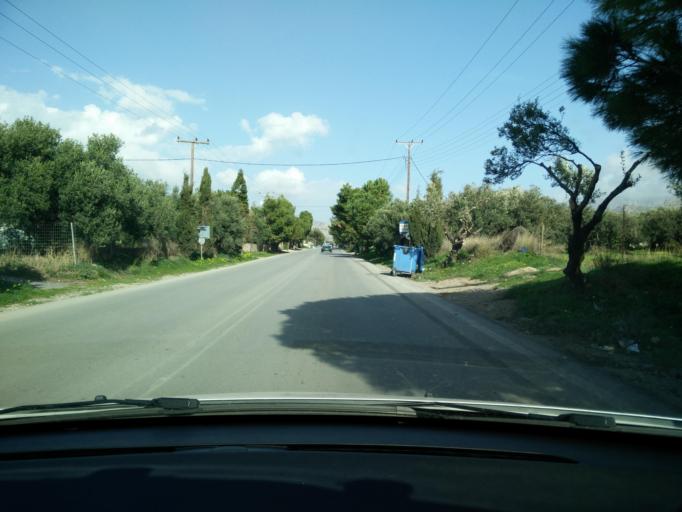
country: GR
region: Crete
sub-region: Nomos Lasithiou
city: Ierapetra
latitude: 35.0185
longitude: 25.7481
